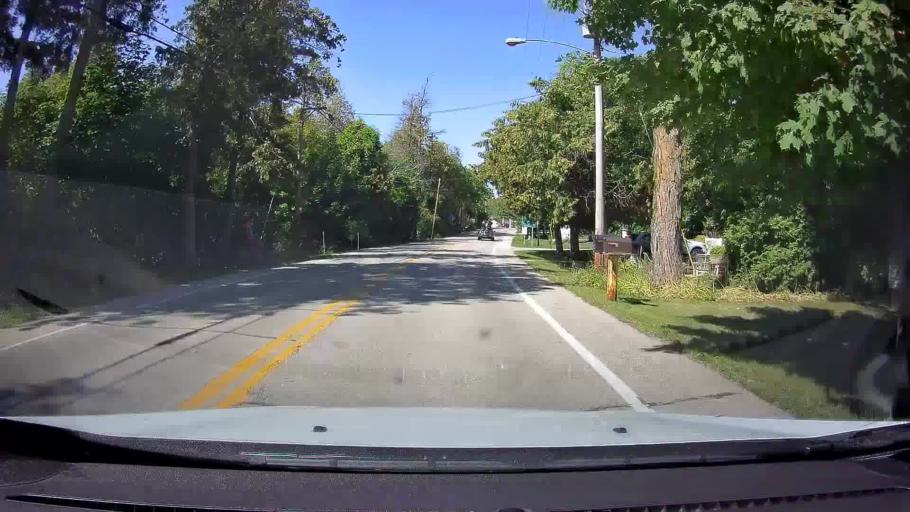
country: US
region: Michigan
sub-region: Delta County
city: Escanaba
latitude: 45.2891
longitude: -87.0218
